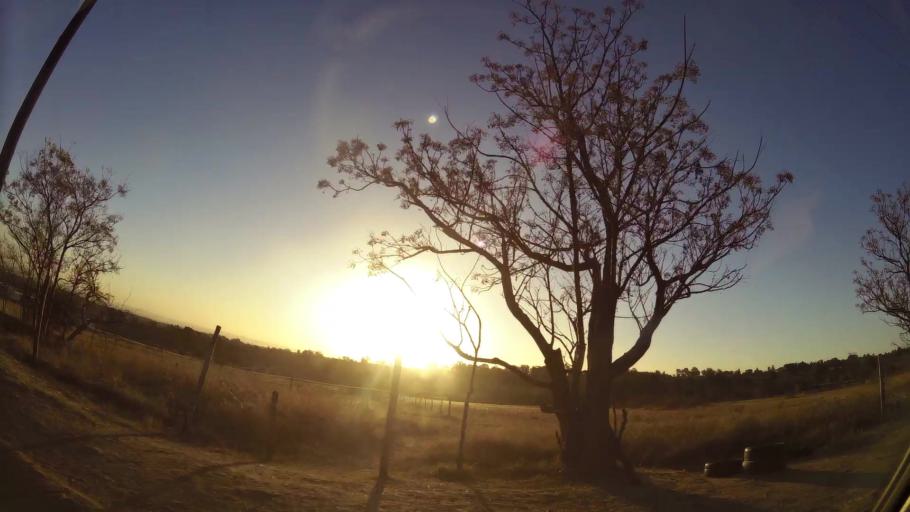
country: ZA
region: Gauteng
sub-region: City of Johannesburg Metropolitan Municipality
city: Diepsloot
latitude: -25.9392
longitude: 28.0420
